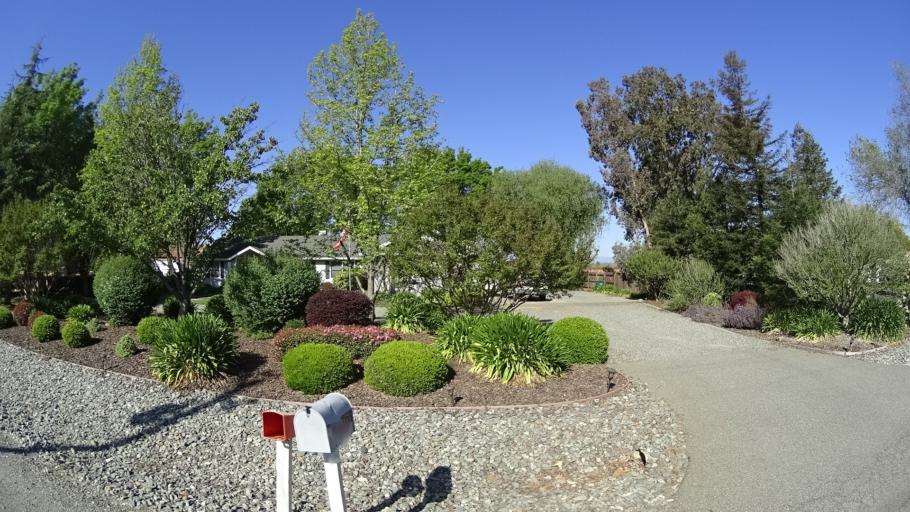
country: US
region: California
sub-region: Glenn County
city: Willows
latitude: 39.5434
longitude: -122.1982
